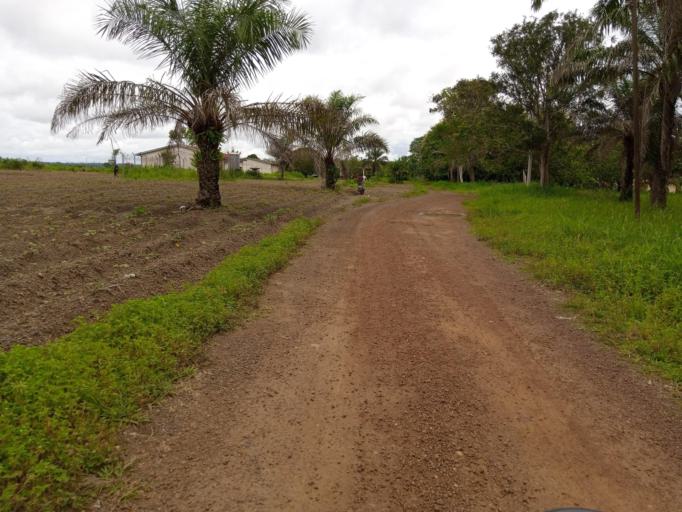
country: SL
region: Southern Province
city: Moyamba
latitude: 8.1700
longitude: -12.4194
